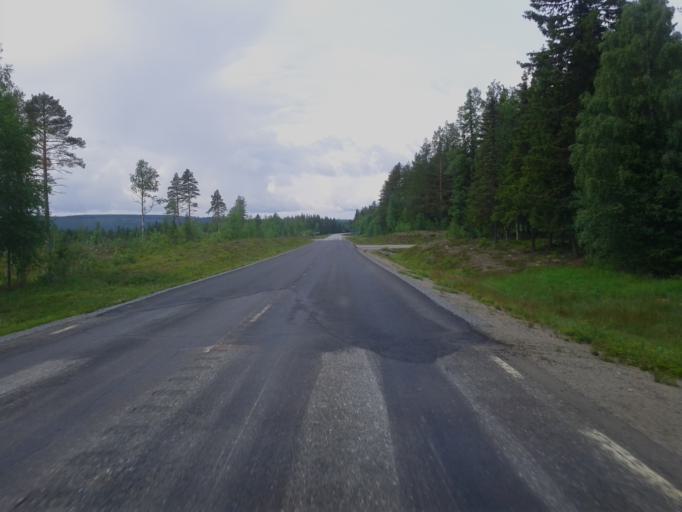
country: SE
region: Vaesterbotten
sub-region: Norsjo Kommun
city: Norsjoe
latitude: 64.9917
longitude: 19.3092
